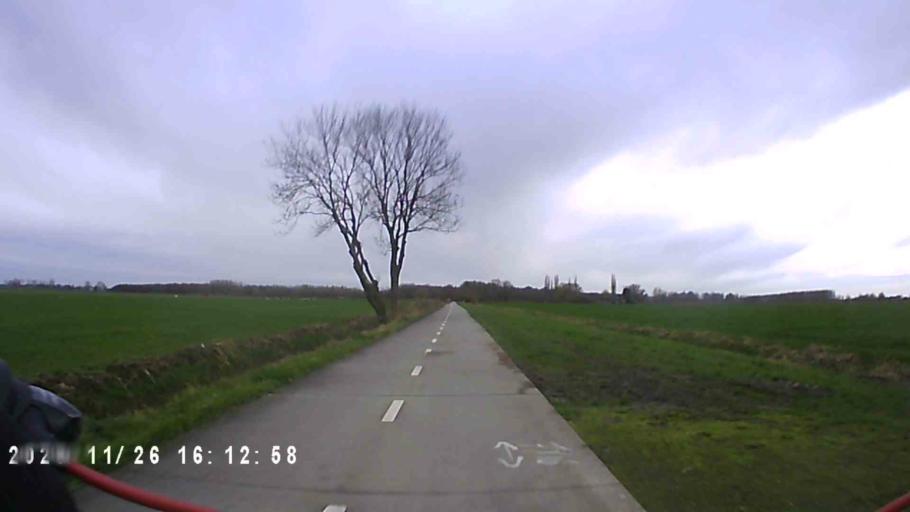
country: NL
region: Groningen
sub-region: Gemeente Groningen
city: Oosterpark
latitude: 53.2484
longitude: 6.6440
